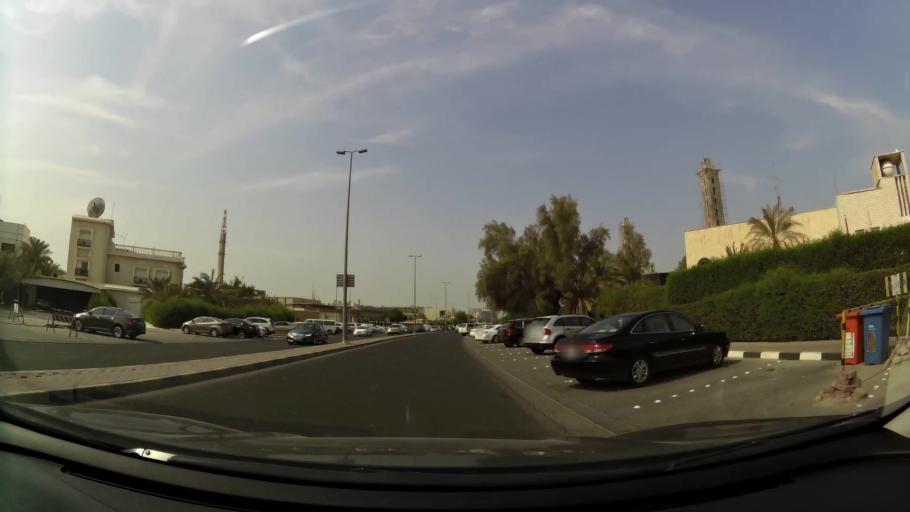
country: KW
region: Al Asimah
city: Ash Shamiyah
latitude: 29.3390
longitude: 47.9539
